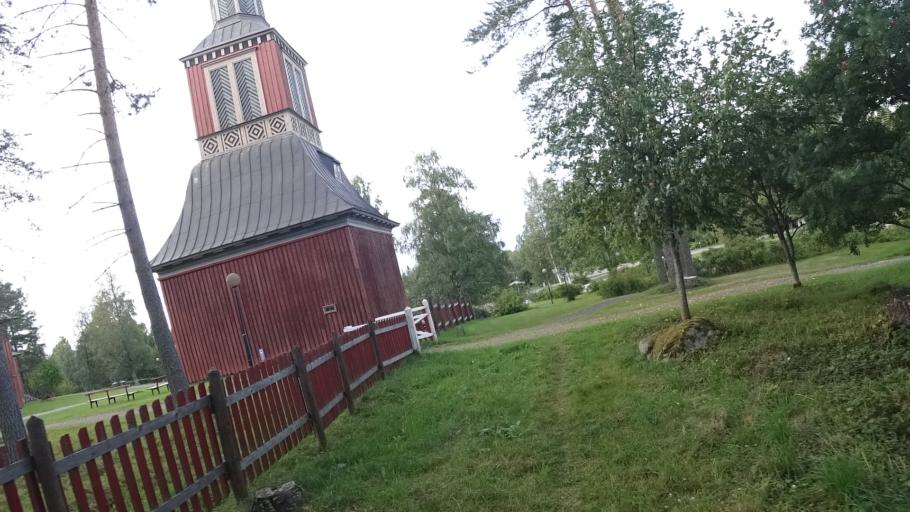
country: FI
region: North Karelia
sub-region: Joensuu
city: Ilomantsi
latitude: 62.6753
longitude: 30.9158
